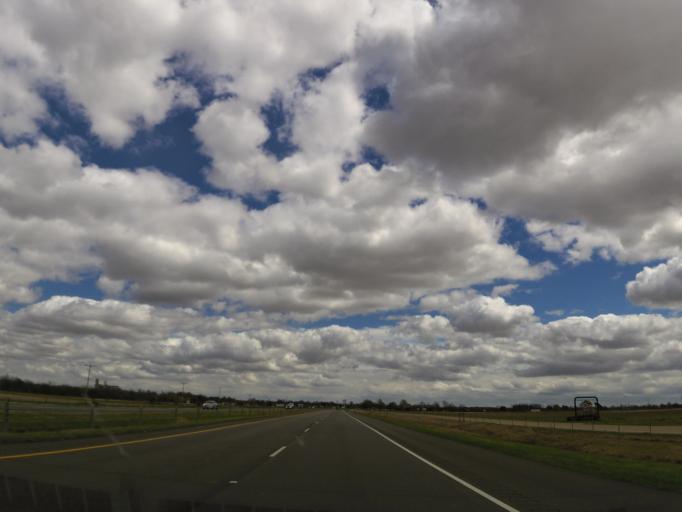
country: US
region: Arkansas
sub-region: Poinsett County
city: Marked Tree
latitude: 35.5278
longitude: -90.4494
